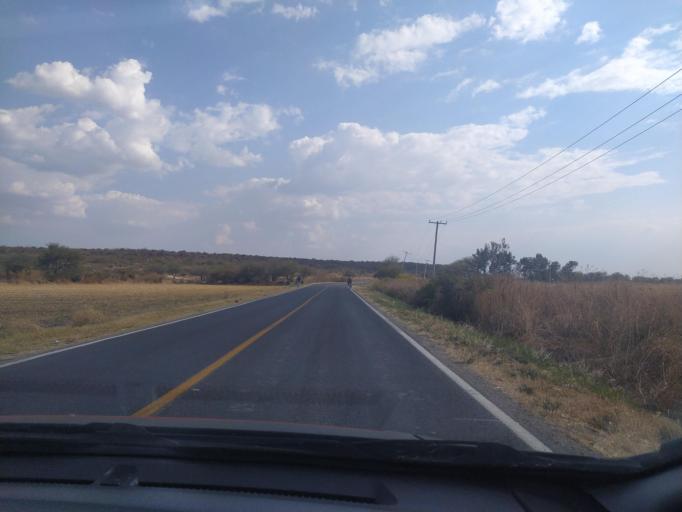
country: MX
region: Guanajuato
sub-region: San Francisco del Rincon
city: San Ignacio de Hidalgo
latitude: 20.9302
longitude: -101.8521
